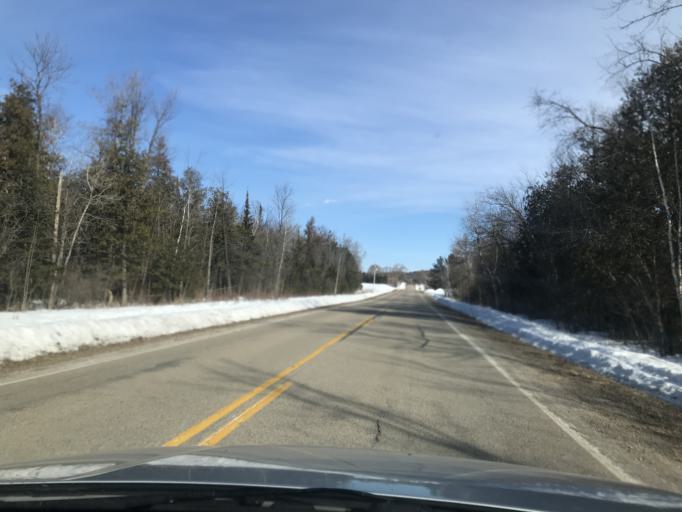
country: US
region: Wisconsin
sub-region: Oconto County
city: Gillett
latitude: 44.9550
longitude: -88.2651
